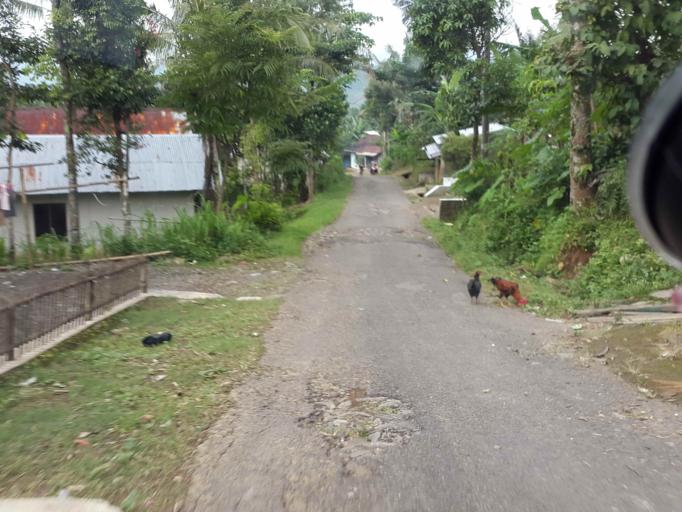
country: ID
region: Central Java
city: Randudongkal
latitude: -7.1535
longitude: 109.3390
